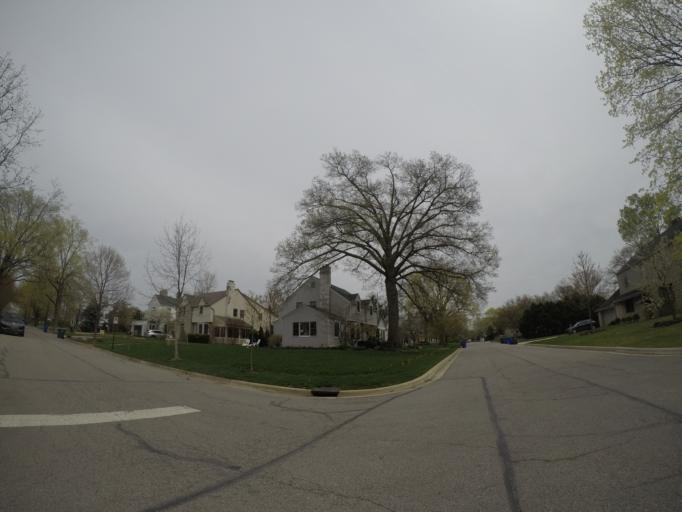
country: US
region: Ohio
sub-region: Franklin County
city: Upper Arlington
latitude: 40.0100
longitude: -83.0675
